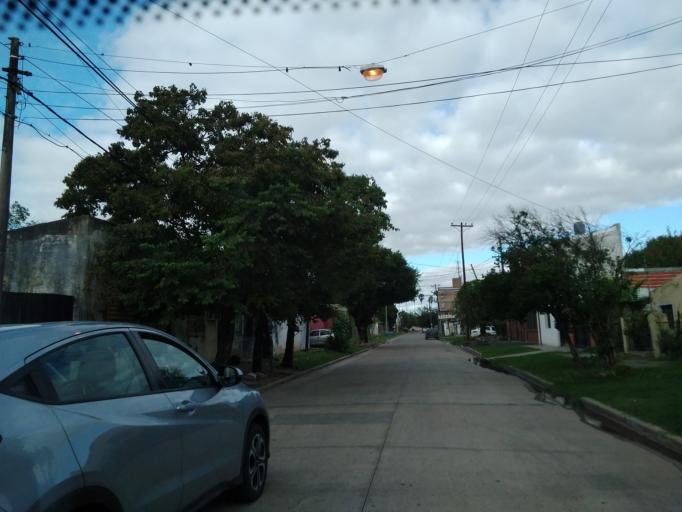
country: AR
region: Corrientes
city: Corrientes
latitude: -27.4765
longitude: -58.8090
